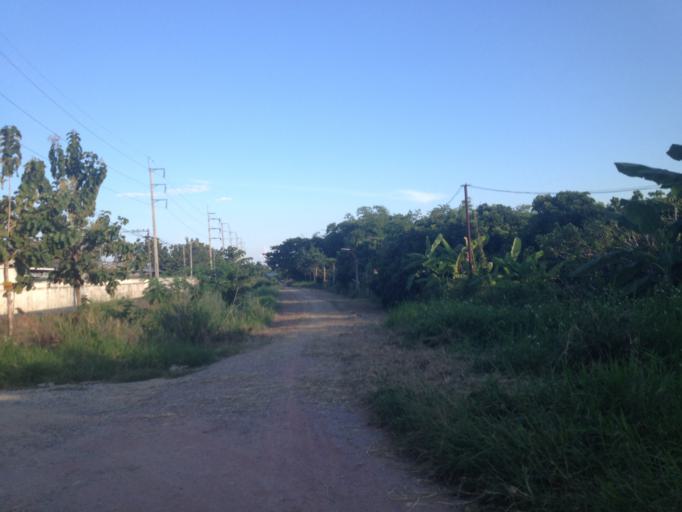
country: TH
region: Chiang Mai
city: Hang Dong
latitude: 18.6791
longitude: 98.8991
